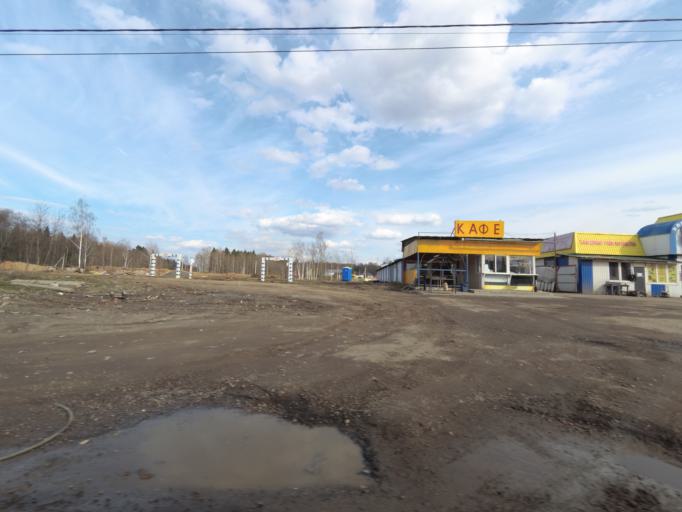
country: RU
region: Moskovskaya
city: Lobnya
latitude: 55.9968
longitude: 37.4215
